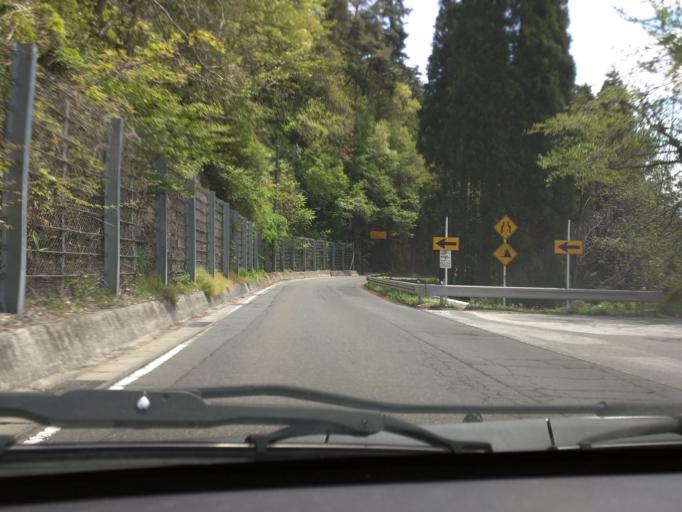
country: JP
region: Nagano
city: Nagano-shi
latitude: 36.6764
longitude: 138.1729
